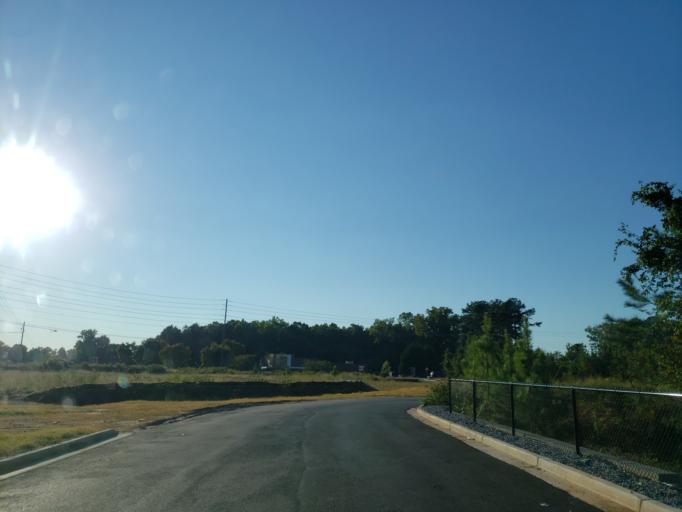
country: US
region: Georgia
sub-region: Cobb County
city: Kennesaw
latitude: 34.0299
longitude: -84.6485
